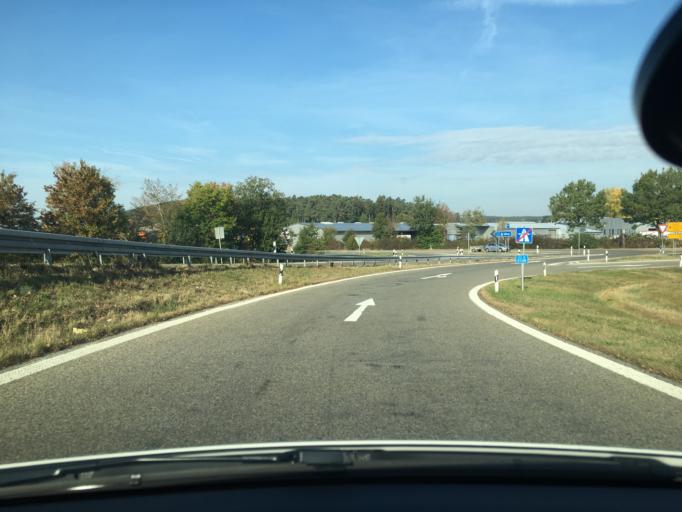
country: DE
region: Bavaria
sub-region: Regierungsbezirk Mittelfranken
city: Petersaurach
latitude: 49.2792
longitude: 10.7171
